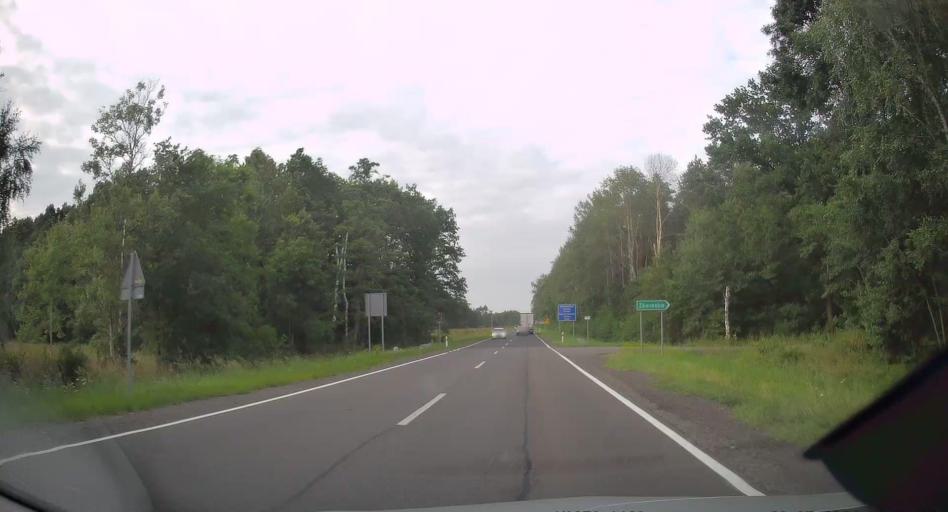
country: PL
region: Lodz Voivodeship
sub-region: Powiat radomszczanski
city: Plawno
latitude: 50.9715
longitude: 19.4080
